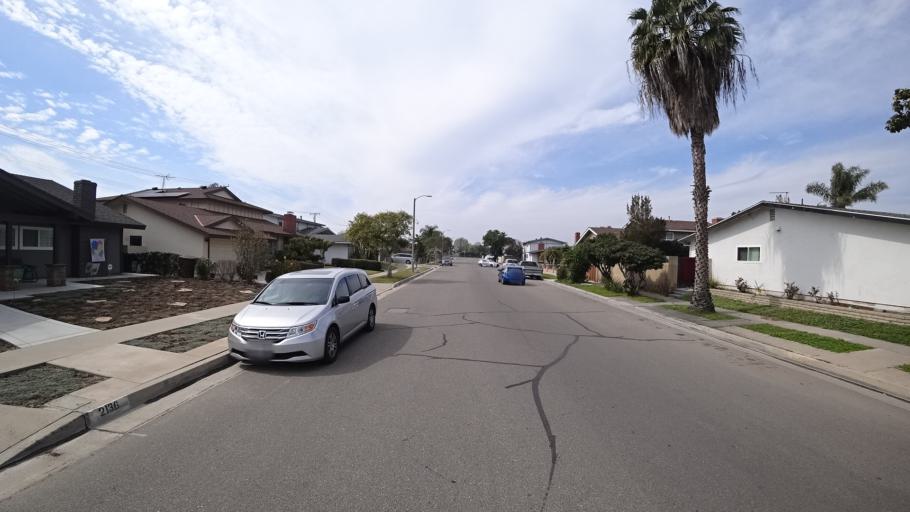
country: US
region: California
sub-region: Orange County
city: Stanton
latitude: 33.8121
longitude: -117.9567
